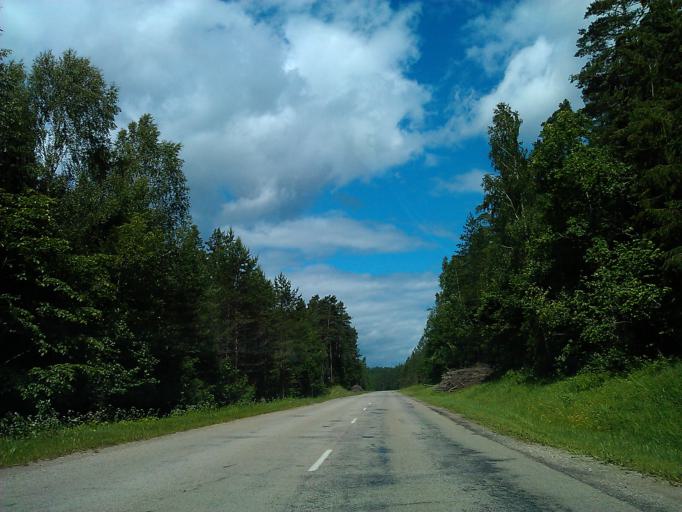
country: LV
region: Talsu Rajons
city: Sabile
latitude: 57.0737
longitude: 22.5331
